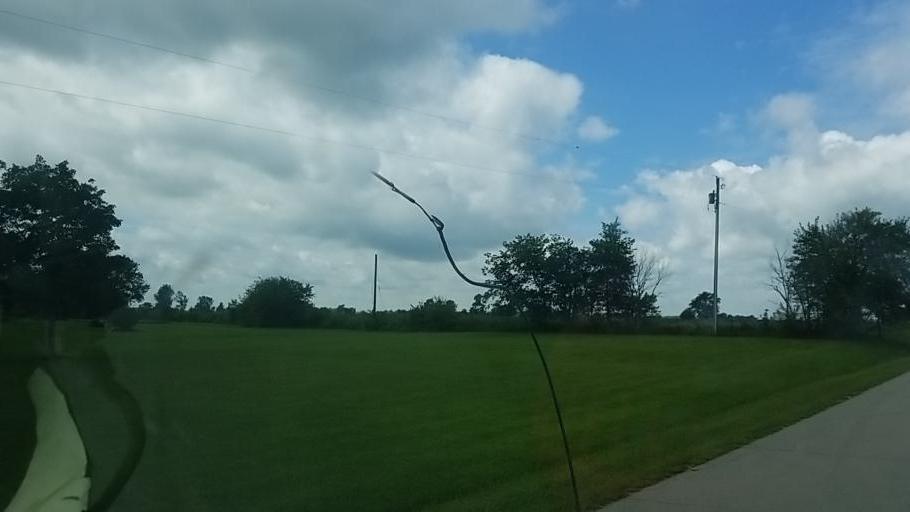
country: US
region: Ohio
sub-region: Fayette County
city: Jeffersonville
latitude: 39.6845
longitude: -83.4872
